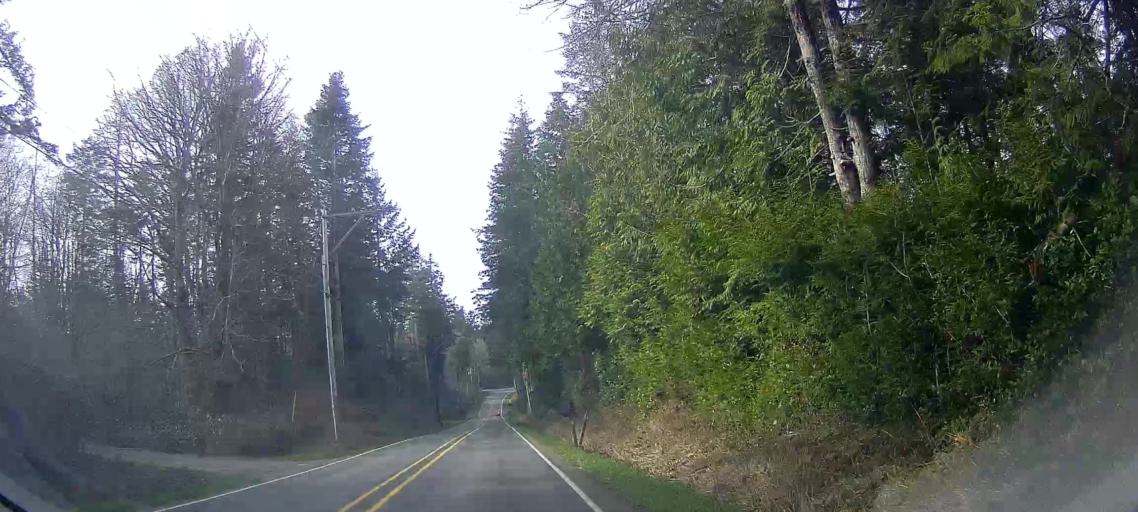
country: US
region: Washington
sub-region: Island County
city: Camano
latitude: 48.1389
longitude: -122.5013
